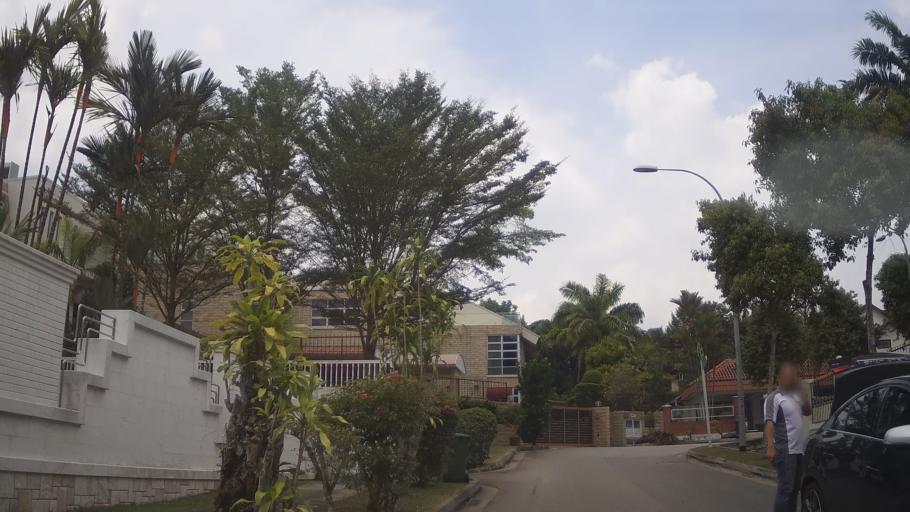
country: MY
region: Johor
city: Johor Bahru
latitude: 1.3696
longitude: 103.7723
